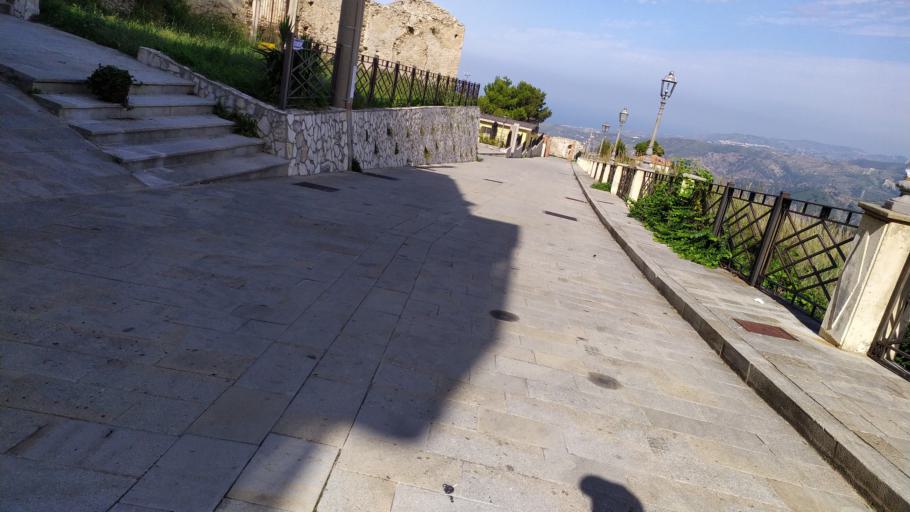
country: IT
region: Sicily
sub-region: Messina
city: Rometta
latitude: 38.1724
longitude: 15.4159
